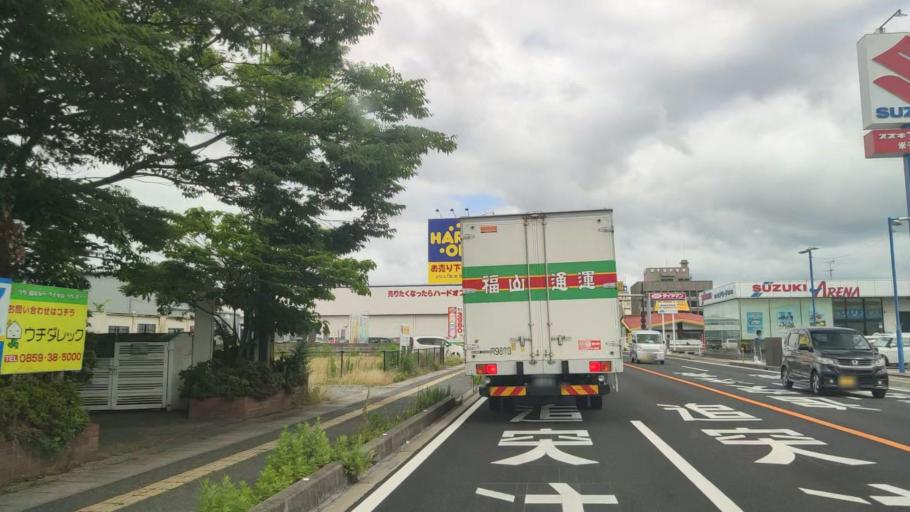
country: JP
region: Tottori
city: Yonago
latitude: 35.4363
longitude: 133.3459
